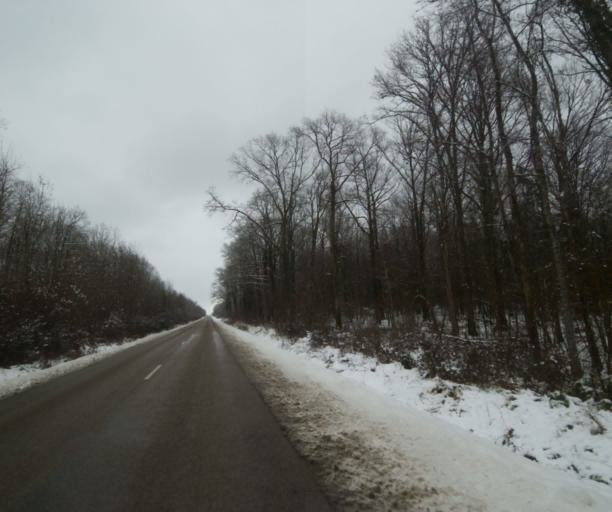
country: FR
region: Champagne-Ardenne
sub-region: Departement de la Haute-Marne
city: Laneuville-a-Remy
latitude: 48.4940
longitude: 4.9055
